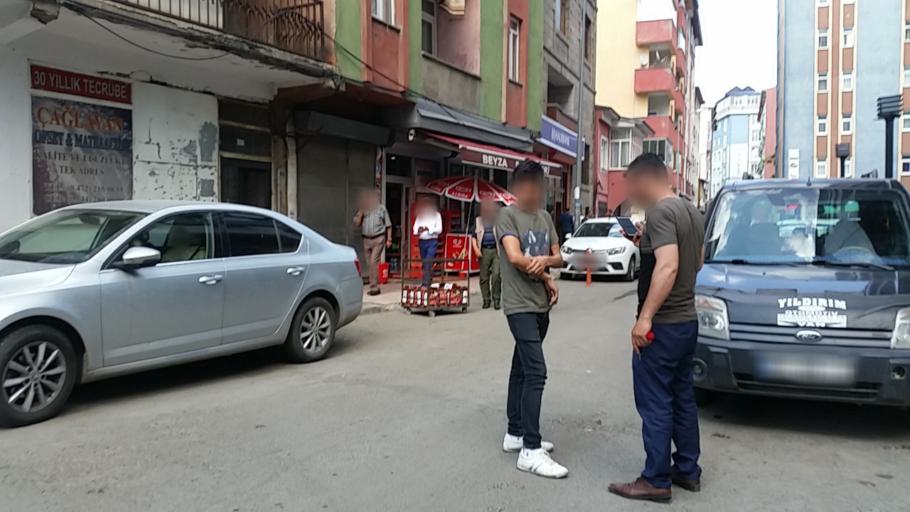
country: TR
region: Agri
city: Agri
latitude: 39.7210
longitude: 43.0537
